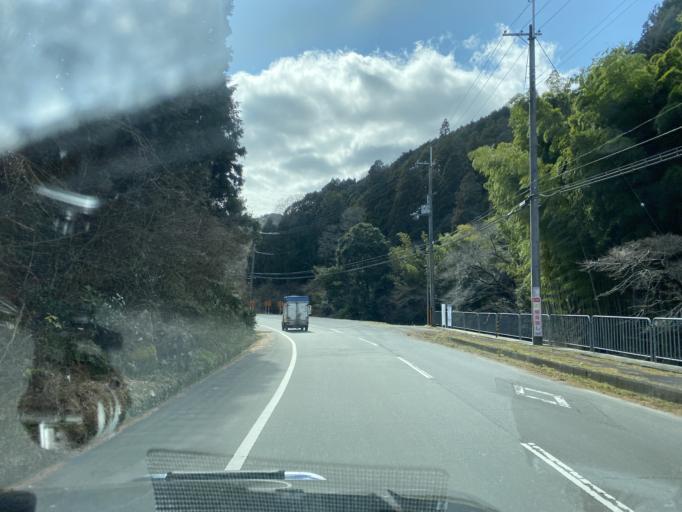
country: JP
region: Nara
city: Nara-shi
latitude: 34.7092
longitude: 135.9500
